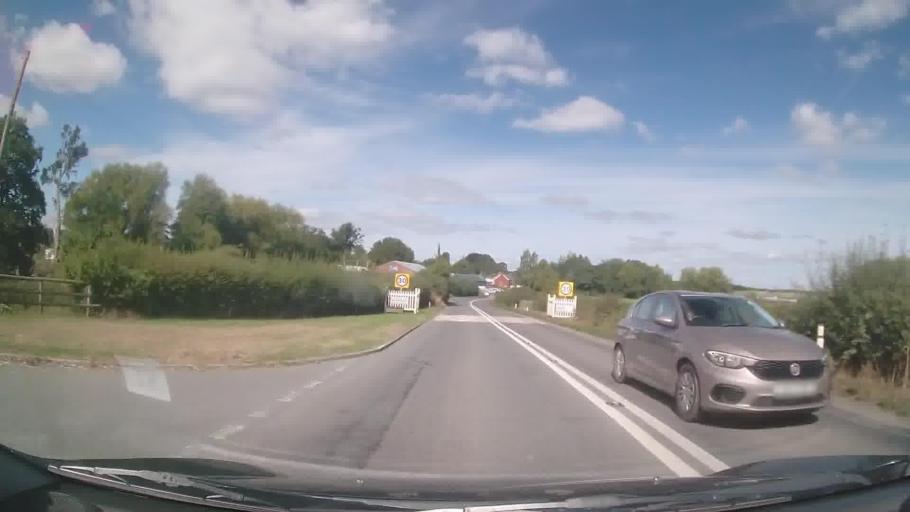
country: GB
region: England
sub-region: Herefordshire
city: Kinnersley
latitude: 52.1320
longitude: -3.0053
